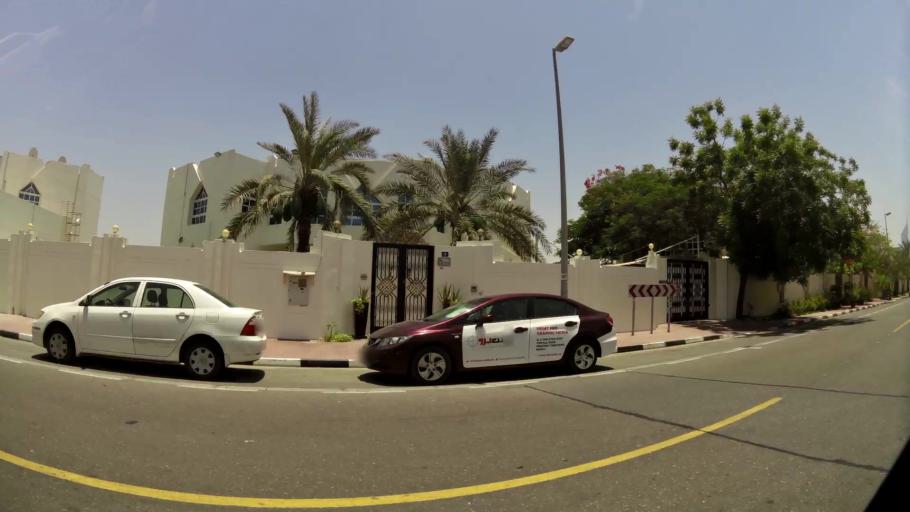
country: AE
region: Ash Shariqah
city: Sharjah
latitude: 25.2397
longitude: 55.2923
